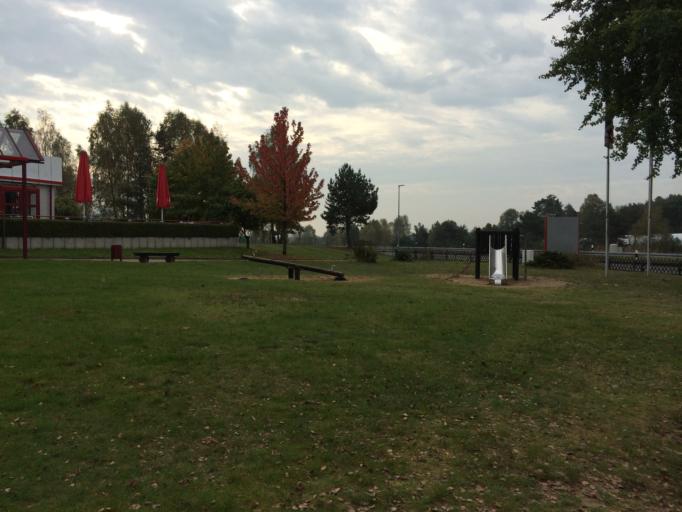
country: DE
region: Brandenburg
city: Walsleben
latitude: 52.9517
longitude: 12.6610
